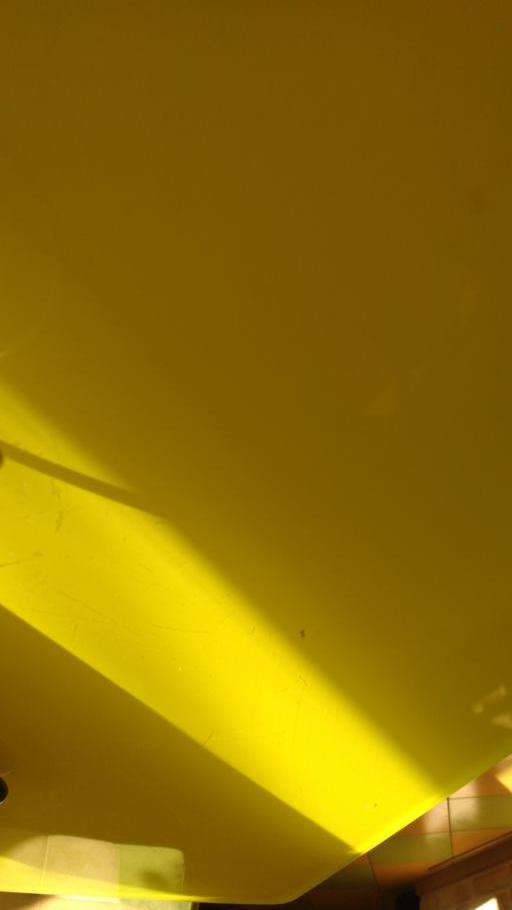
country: RU
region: Moskovskaya
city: Klin
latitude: 56.3616
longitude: 36.6467
